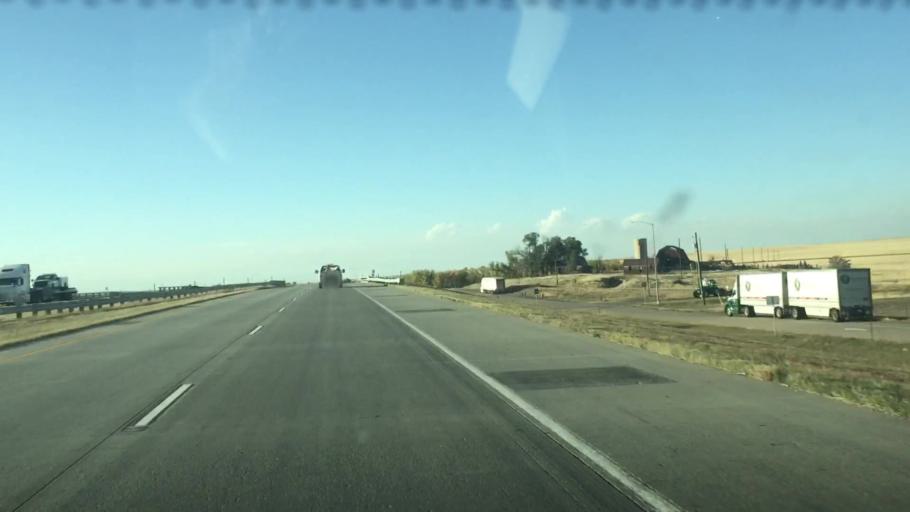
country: US
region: Colorado
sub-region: Arapahoe County
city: Byers
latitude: 39.5046
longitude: -103.9710
